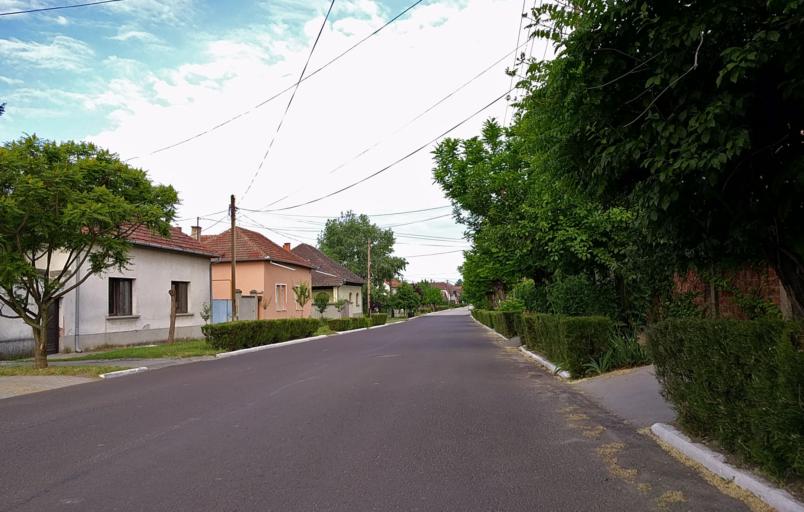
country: HU
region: Bacs-Kiskun
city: Tiszakecske
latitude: 46.9299
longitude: 20.1008
